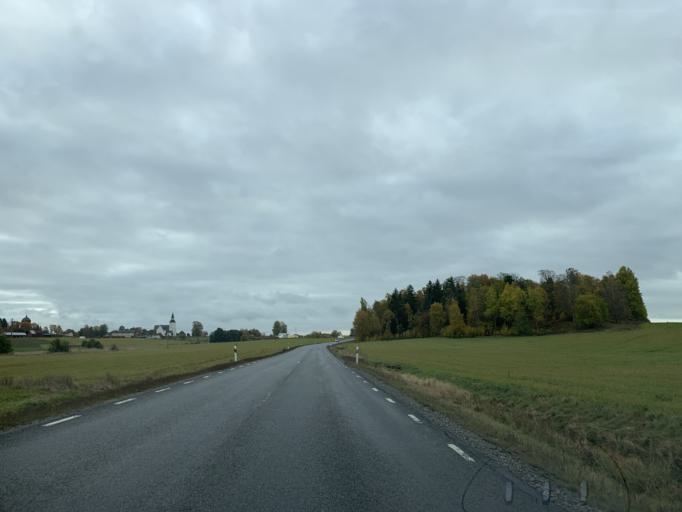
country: SE
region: Stockholm
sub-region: Nynashamns Kommun
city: Osmo
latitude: 59.0157
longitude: 17.8042
